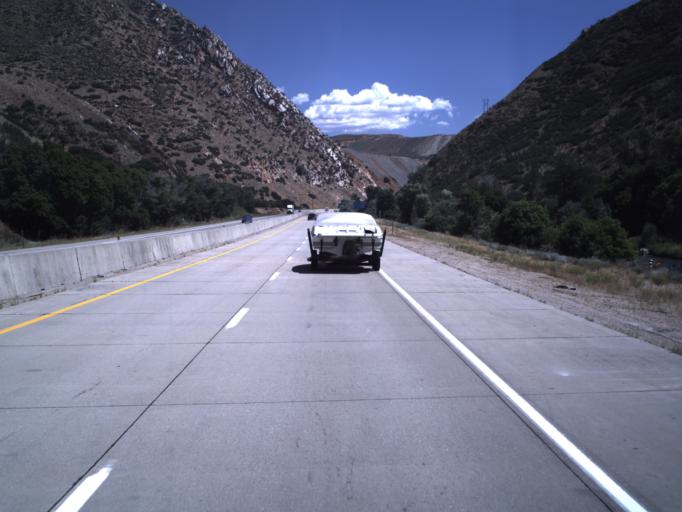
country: US
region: Utah
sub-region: Morgan County
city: Morgan
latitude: 41.0624
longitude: -111.5647
